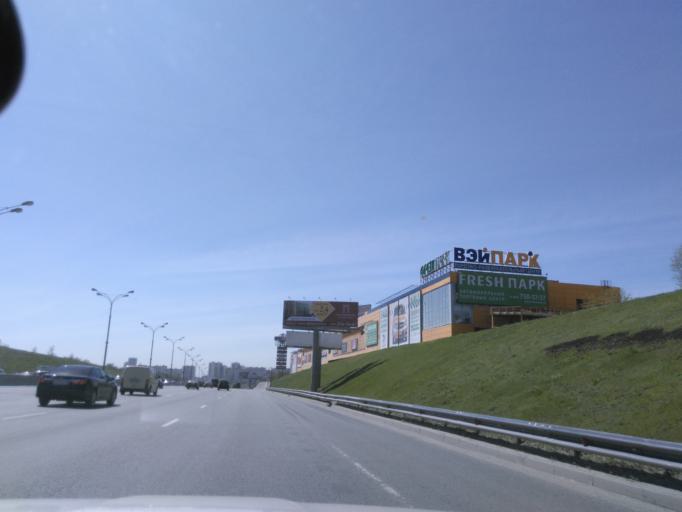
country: RU
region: Moscow
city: Strogino
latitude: 55.8600
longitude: 37.3979
